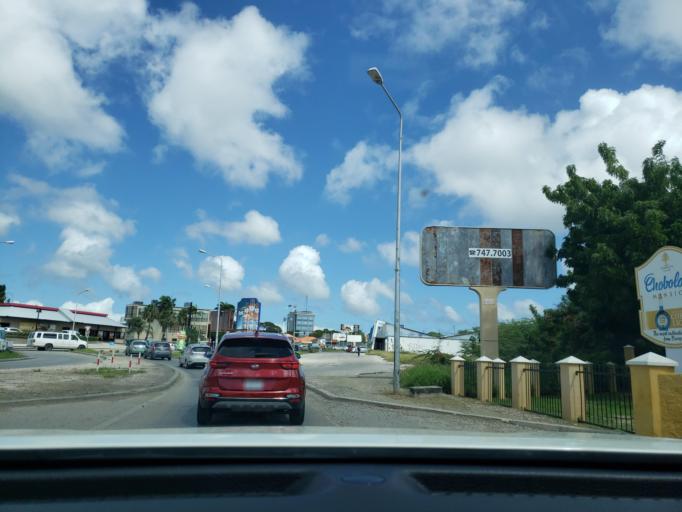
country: CW
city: Willemstad
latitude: 12.1104
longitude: -68.9047
